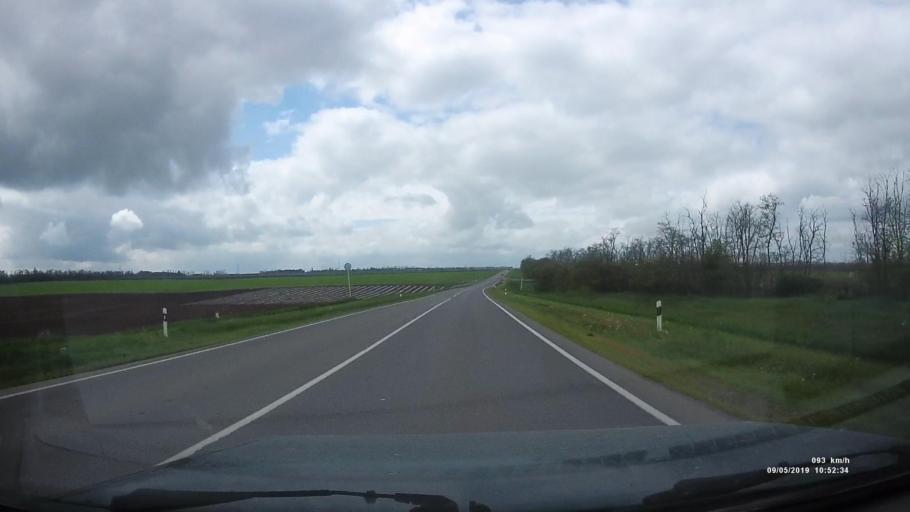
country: RU
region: Rostov
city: Peshkovo
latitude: 46.8992
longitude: 39.3519
